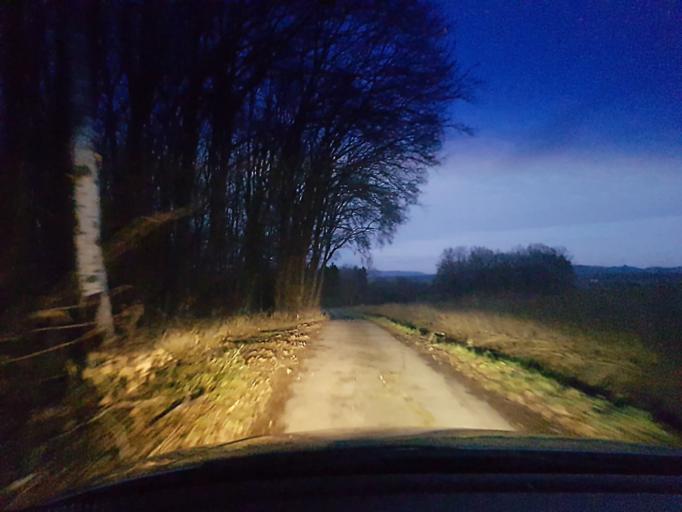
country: DE
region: Bavaria
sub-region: Upper Franconia
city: Memmelsdorf
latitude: 49.9406
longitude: 10.9828
